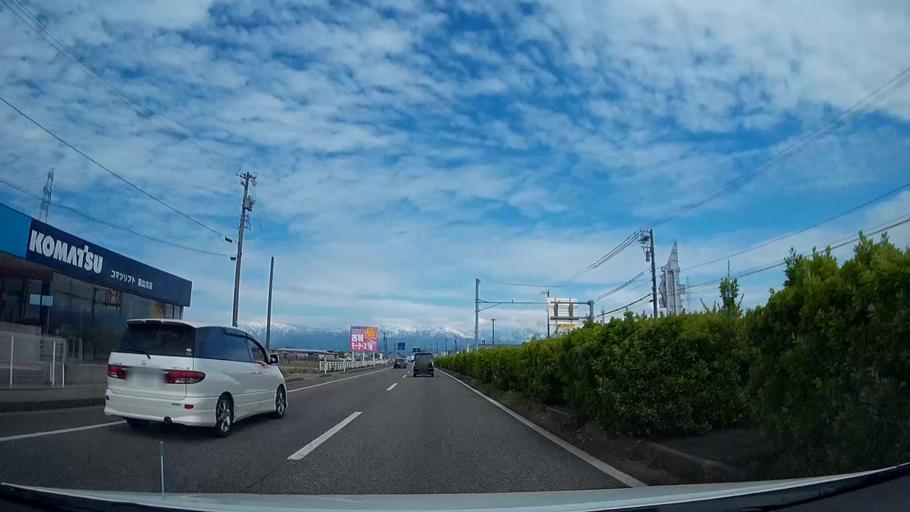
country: JP
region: Toyama
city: Toyama-shi
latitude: 36.7210
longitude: 137.2535
